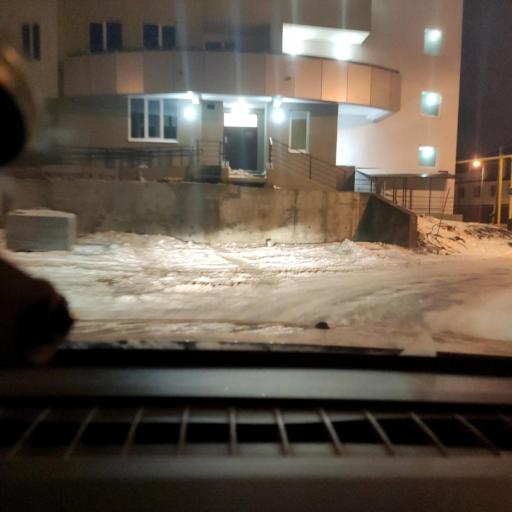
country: RU
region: Samara
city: Samara
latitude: 53.2269
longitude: 50.1537
